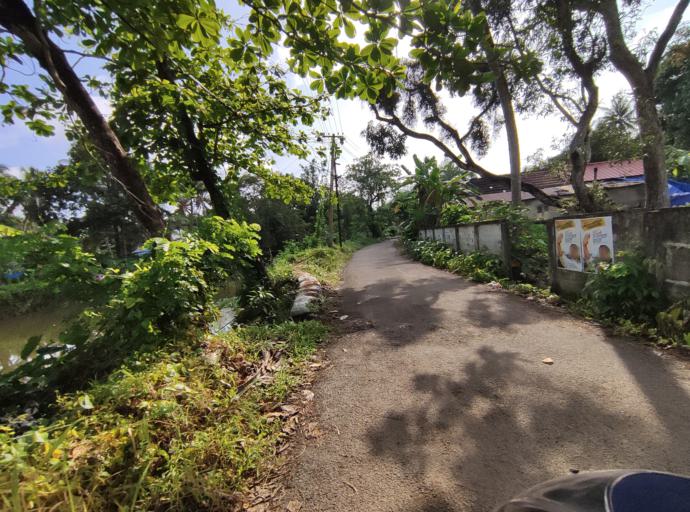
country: IN
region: Kerala
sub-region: Kottayam
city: Kottayam
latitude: 9.5958
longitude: 76.4649
